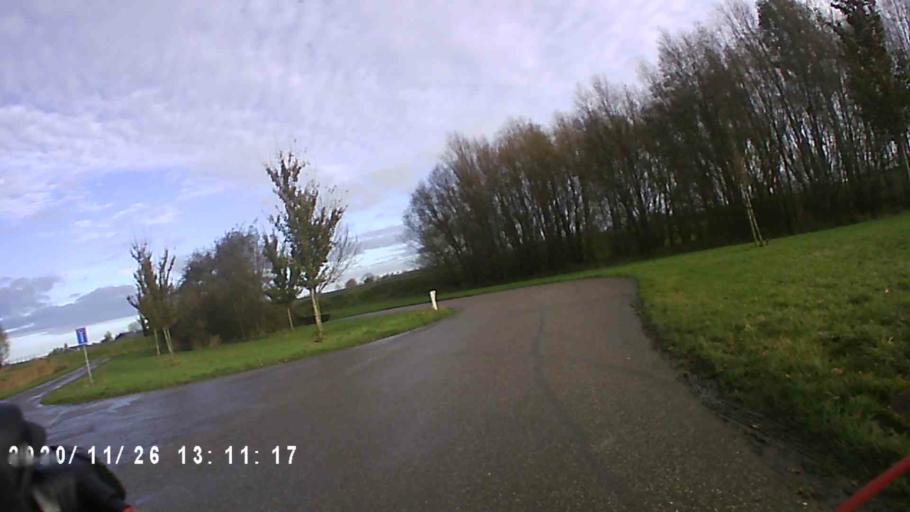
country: NL
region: Groningen
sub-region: Gemeente Appingedam
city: Appingedam
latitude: 53.3537
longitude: 6.8621
